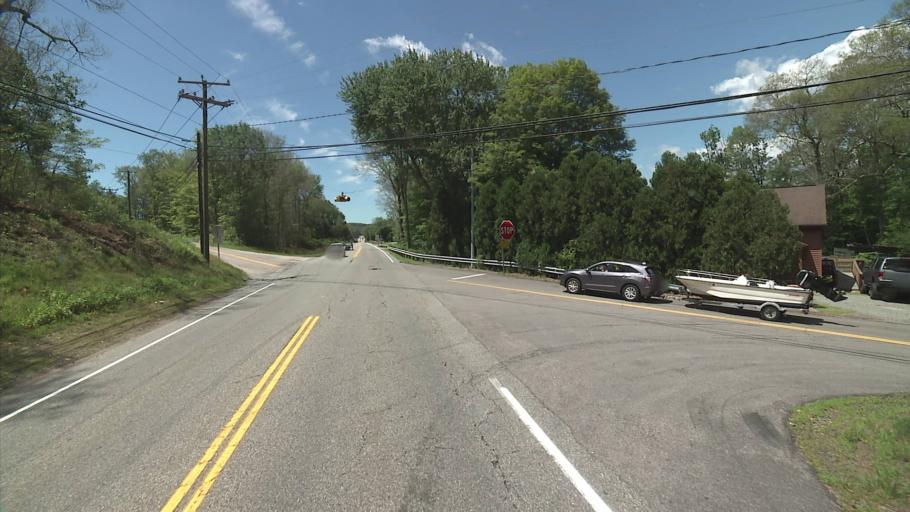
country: US
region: Connecticut
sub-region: New London County
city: Old Mystic
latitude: 41.3993
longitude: -71.9552
